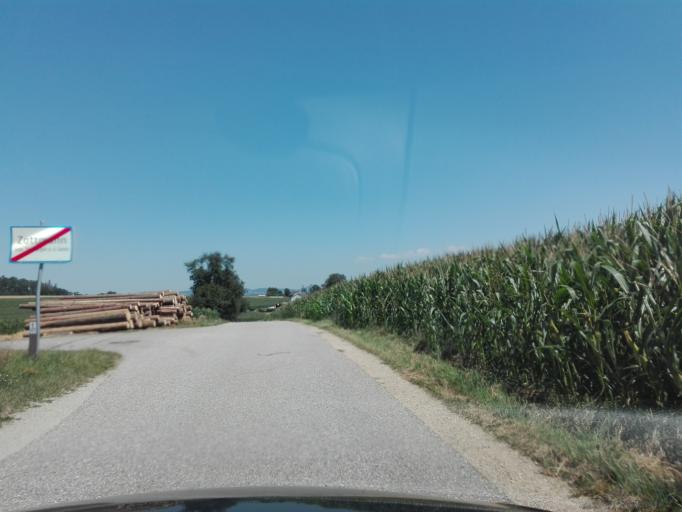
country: AT
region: Upper Austria
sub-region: Politischer Bezirk Urfahr-Umgebung
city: Engerwitzdorf
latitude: 48.2916
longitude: 14.4541
